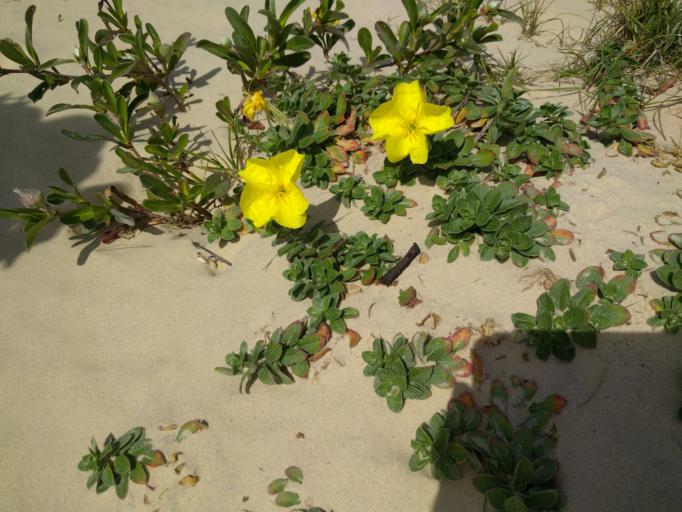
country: AU
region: Queensland
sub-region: Gympie Regional Council
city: Rainbow Beach
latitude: -25.7470
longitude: 153.0868
